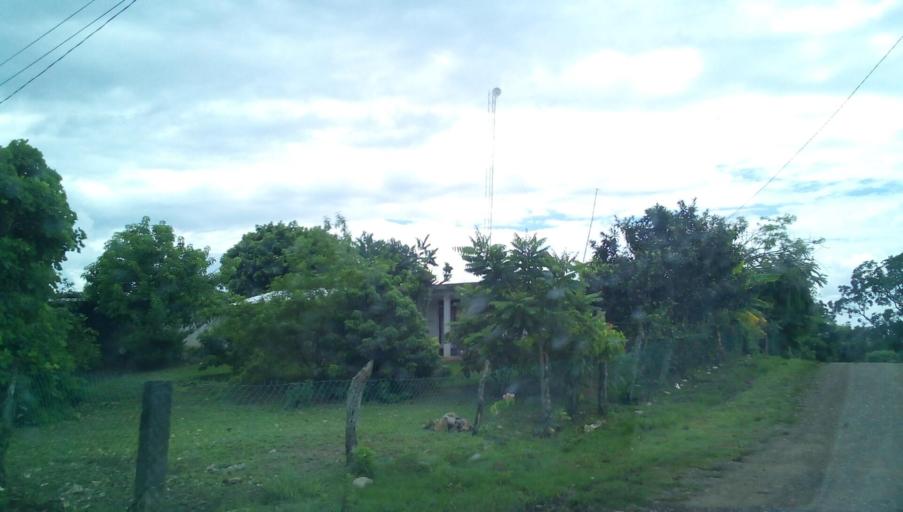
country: MX
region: Veracruz
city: Tepetzintla
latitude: 21.1273
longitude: -97.8580
